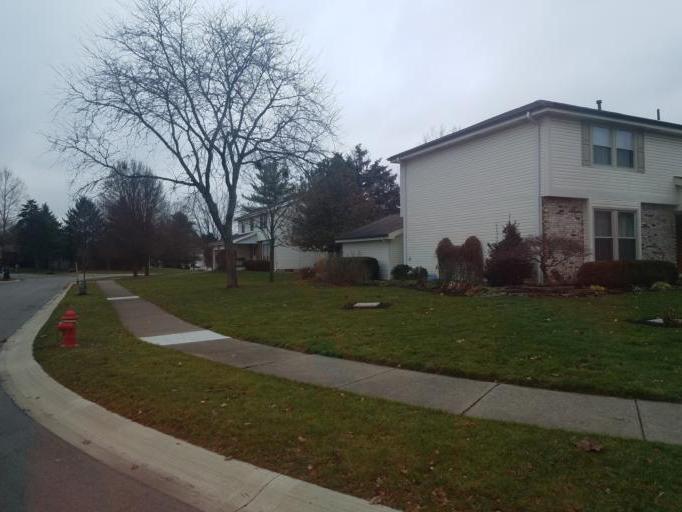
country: US
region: Ohio
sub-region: Franklin County
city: Westerville
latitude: 40.1315
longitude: -82.9671
